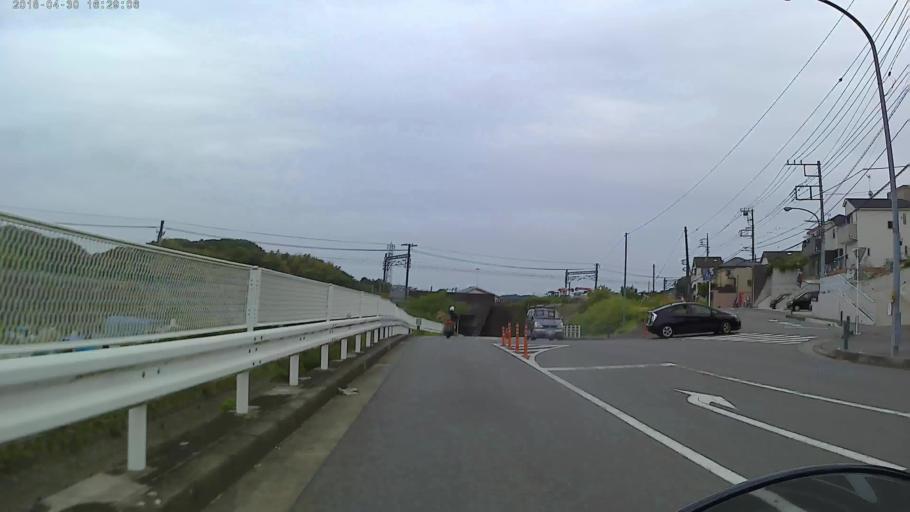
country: JP
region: Kanagawa
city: Zama
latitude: 35.4599
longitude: 139.4052
